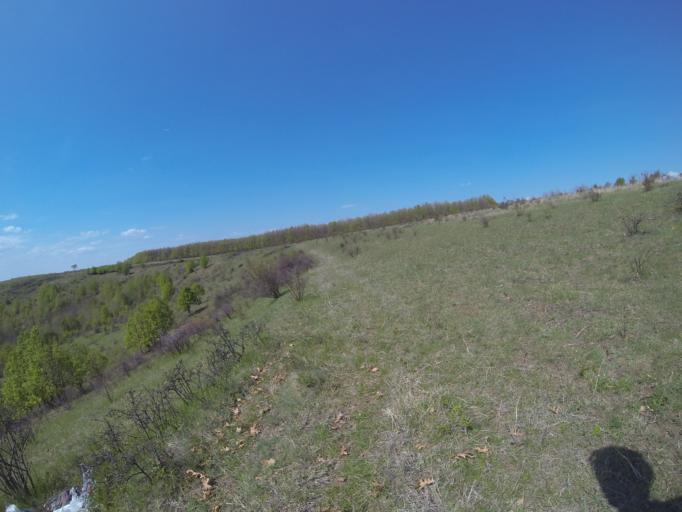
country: RO
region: Gorj
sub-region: Comuna Crusetu
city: Crusetu
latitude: 44.6098
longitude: 23.6488
